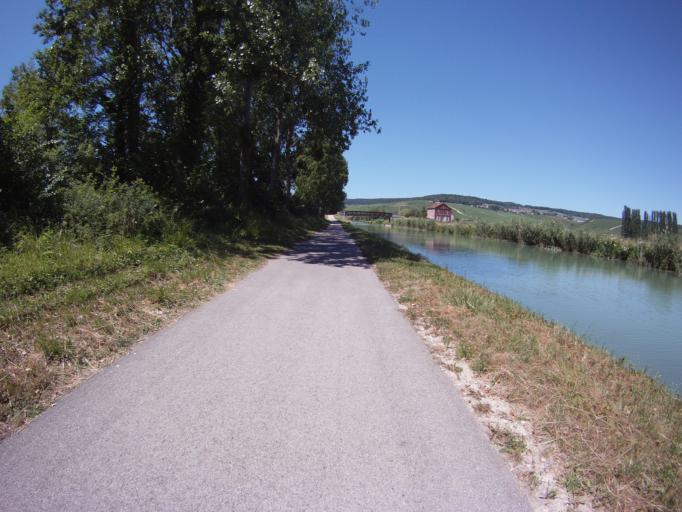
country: FR
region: Champagne-Ardenne
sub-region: Departement de la Marne
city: Dizy
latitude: 49.0661
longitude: 3.9511
